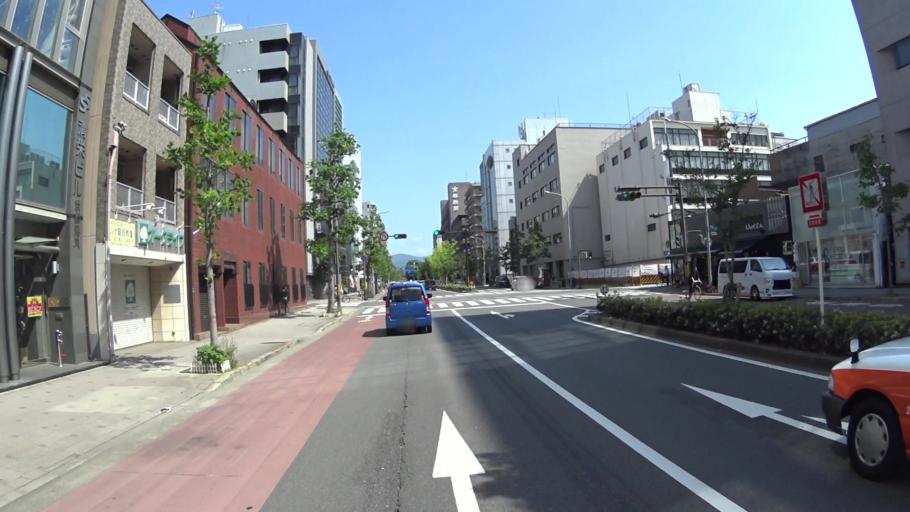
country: JP
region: Kyoto
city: Kyoto
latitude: 35.0132
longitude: 135.7597
